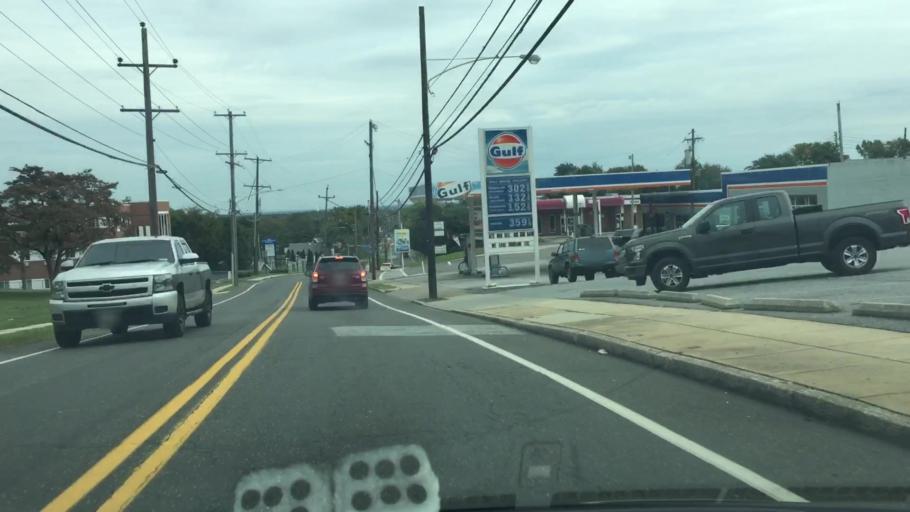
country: US
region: Pennsylvania
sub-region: Delaware County
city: Village Green-Green Ridge
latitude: 39.8651
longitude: -75.4181
